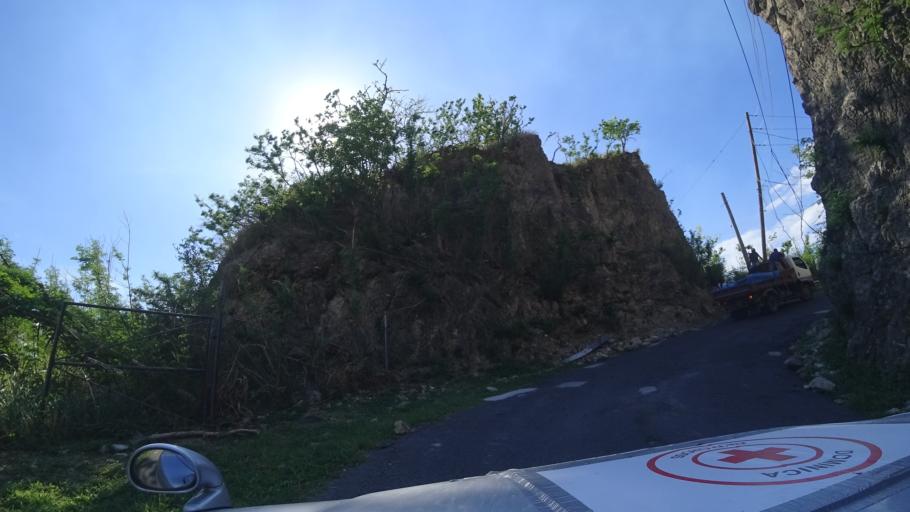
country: DM
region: Saint Mark
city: Soufriere
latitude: 15.2423
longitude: -61.3721
